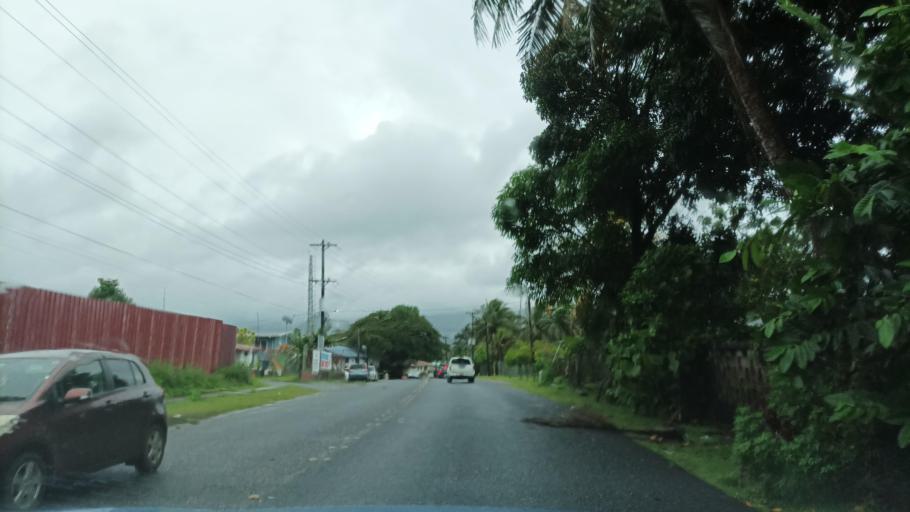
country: FM
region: Pohnpei
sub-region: Kolonia Municipality
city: Kolonia
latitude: 6.9609
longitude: 158.2105
